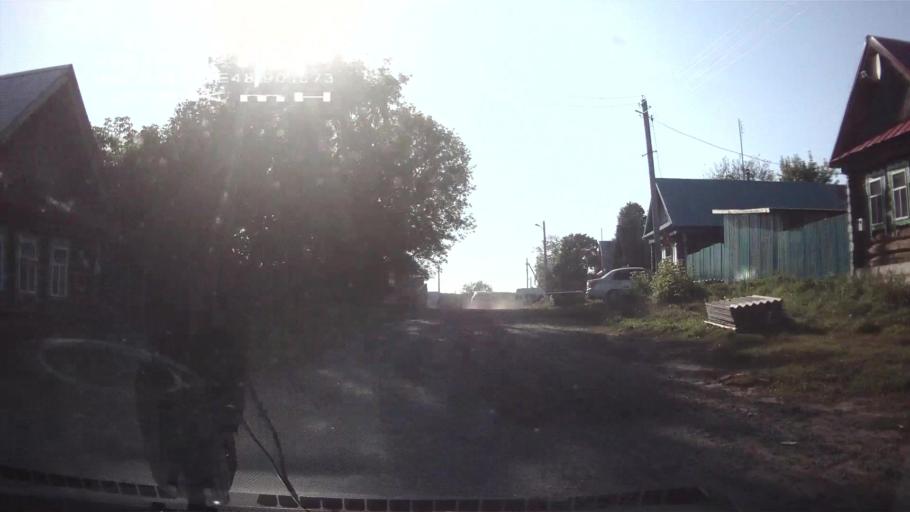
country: RU
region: Mariy-El
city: Morki
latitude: 56.3596
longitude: 48.9012
